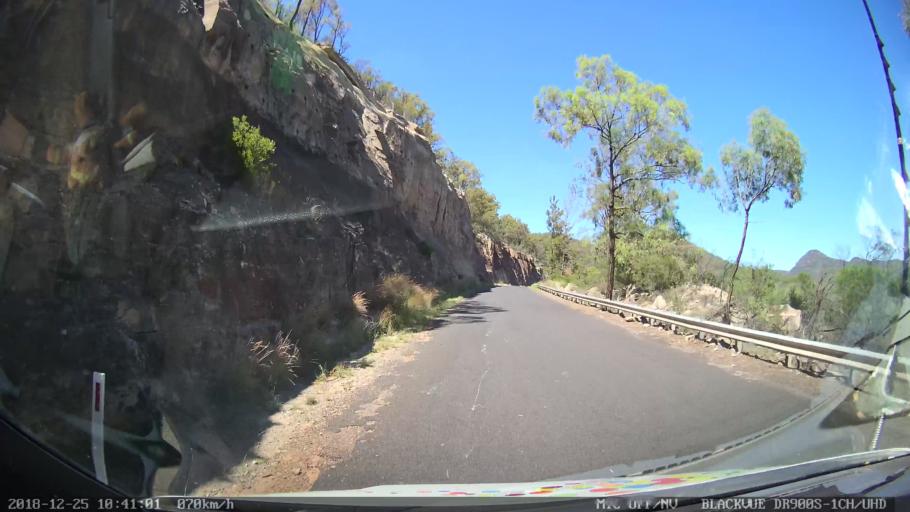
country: AU
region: New South Wales
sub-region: Upper Hunter Shire
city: Merriwa
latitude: -32.4135
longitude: 150.3391
